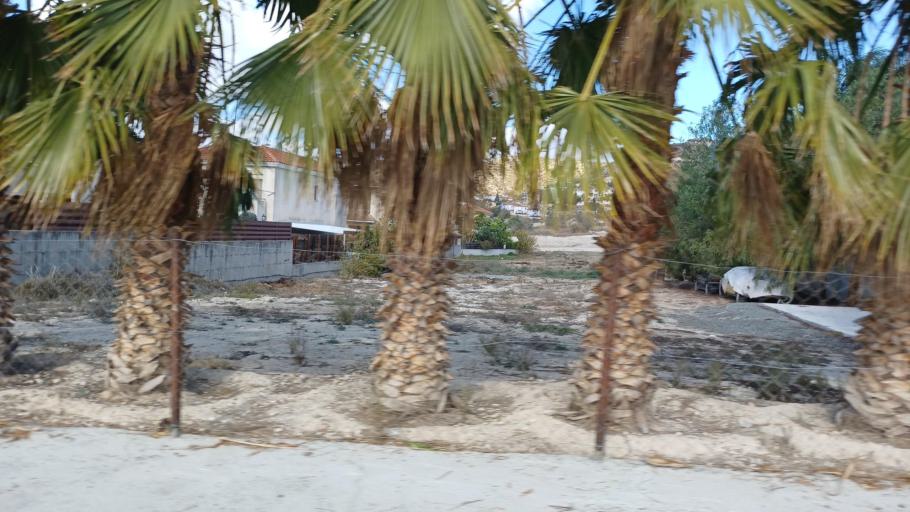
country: CY
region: Limassol
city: Pano Polemidia
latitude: 34.7436
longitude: 33.0043
